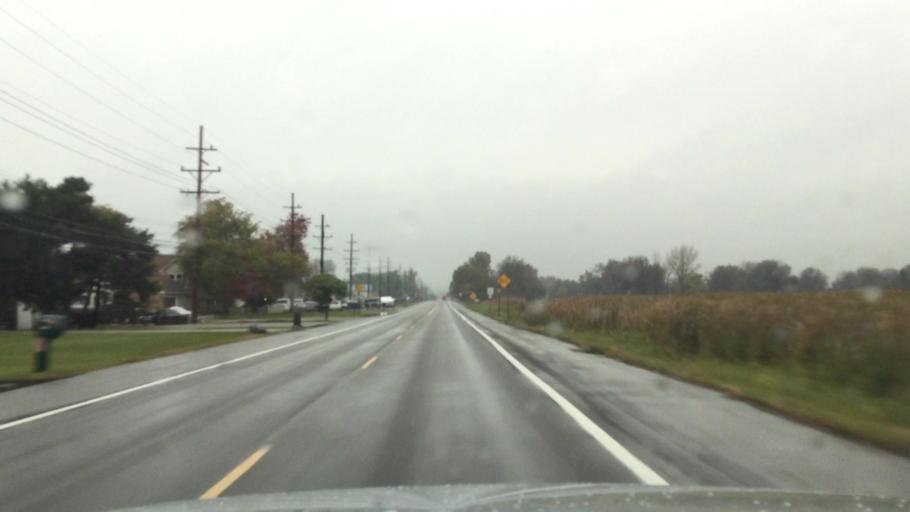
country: US
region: Michigan
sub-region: Saint Clair County
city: Pearl Beach
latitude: 42.6565
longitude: -82.6191
